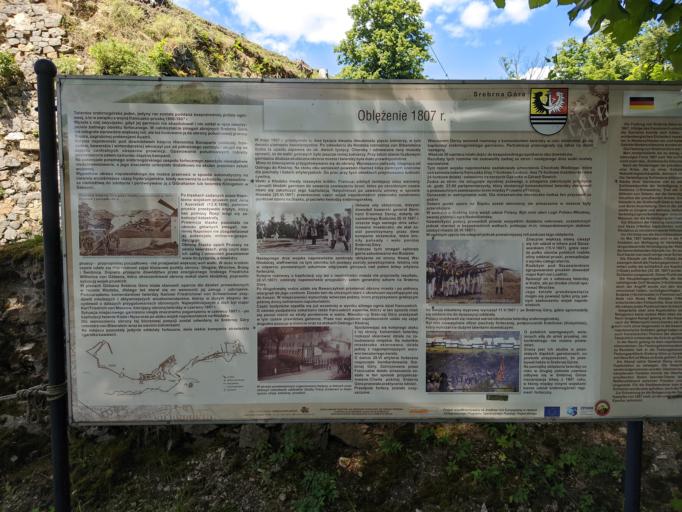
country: PL
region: Lower Silesian Voivodeship
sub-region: Powiat zabkowicki
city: Budzow
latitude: 50.5748
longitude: 16.6442
